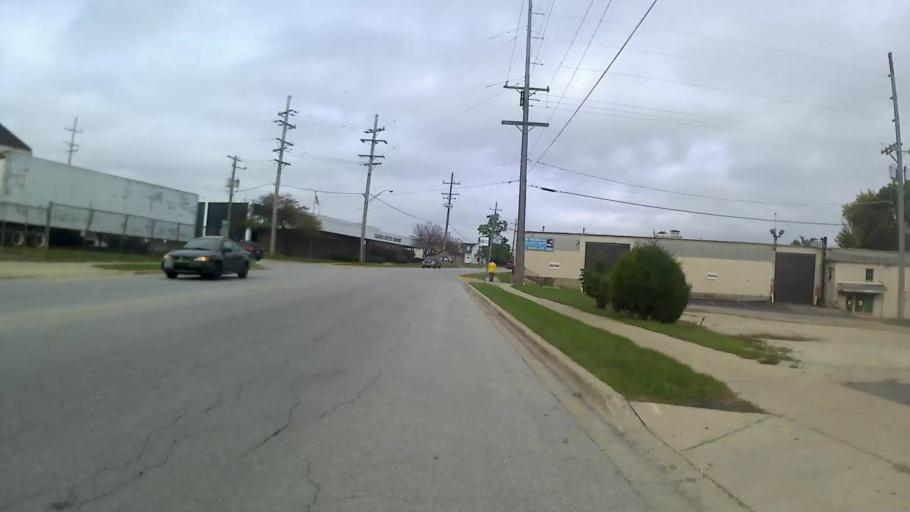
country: US
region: Illinois
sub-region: Kane County
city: Aurora
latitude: 41.7499
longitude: -88.3275
